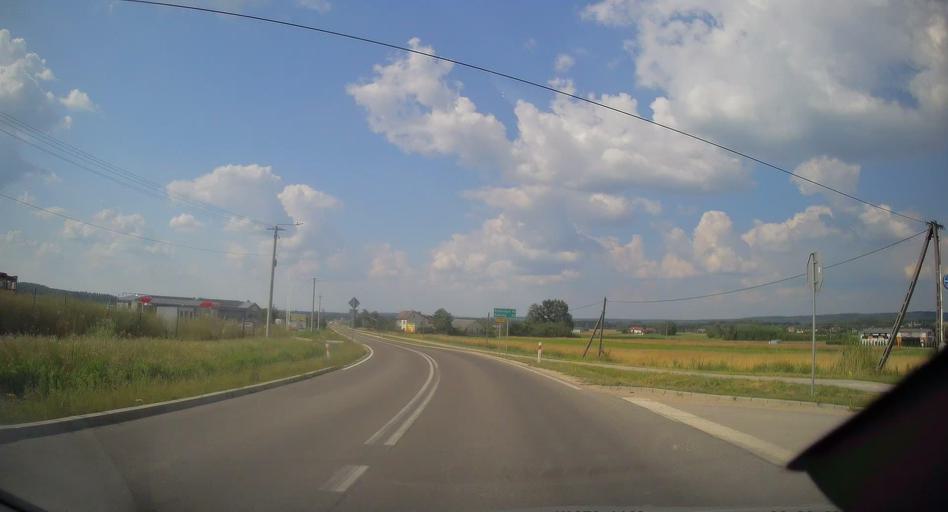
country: PL
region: Swietokrzyskie
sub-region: Powiat kielecki
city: Lopuszno
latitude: 50.9517
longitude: 20.2520
